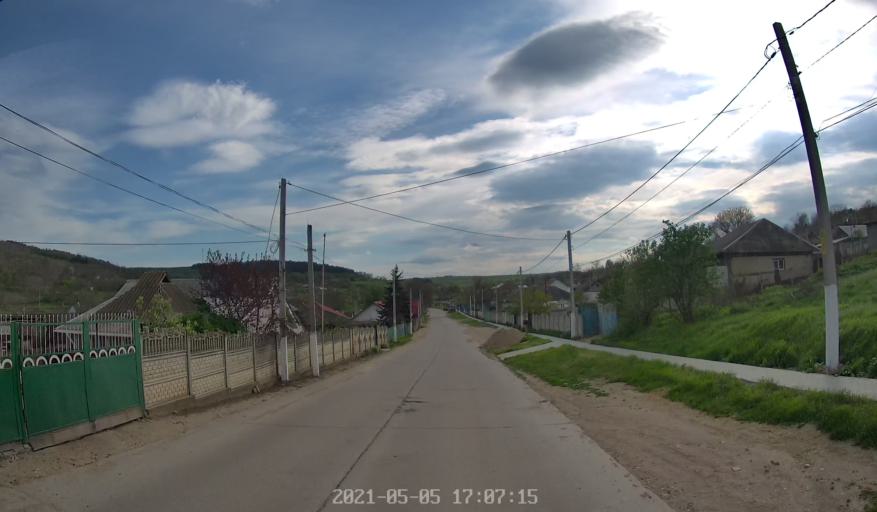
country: MD
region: Chisinau
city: Vadul lui Voda
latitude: 47.0142
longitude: 29.1359
